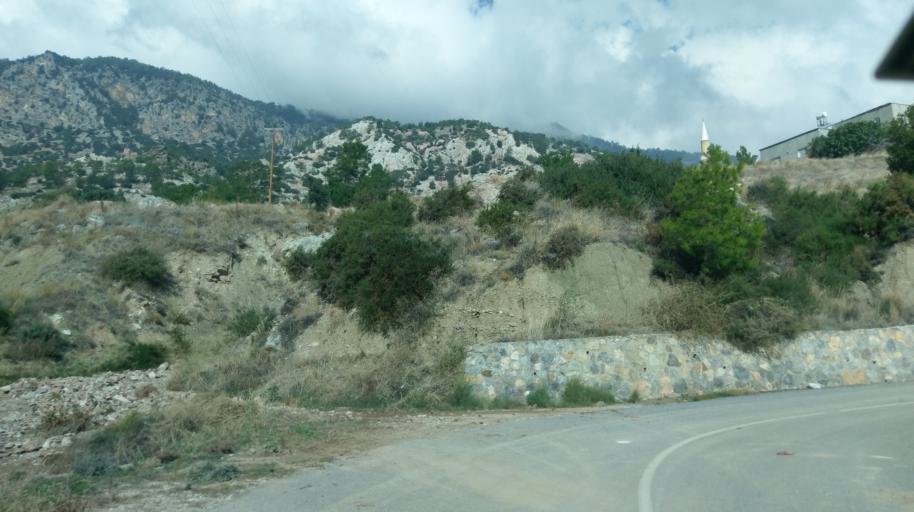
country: CY
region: Ammochostos
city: Lefkonoiko
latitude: 35.3041
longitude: 33.6027
